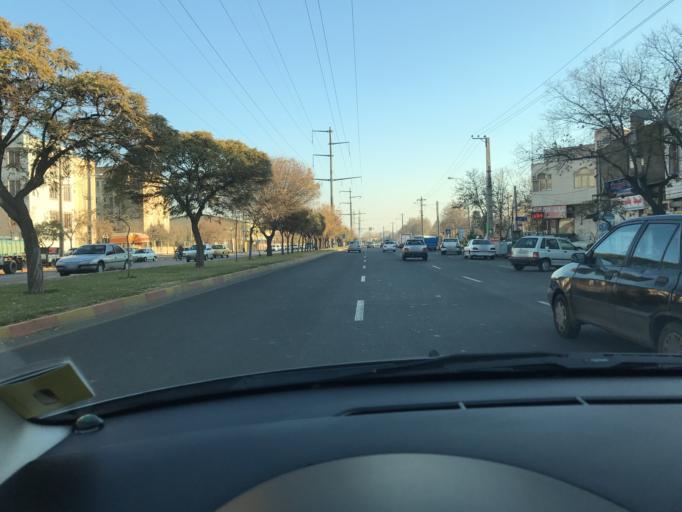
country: IR
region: Qazvin
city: Qazvin
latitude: 36.2924
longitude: 50.0007
